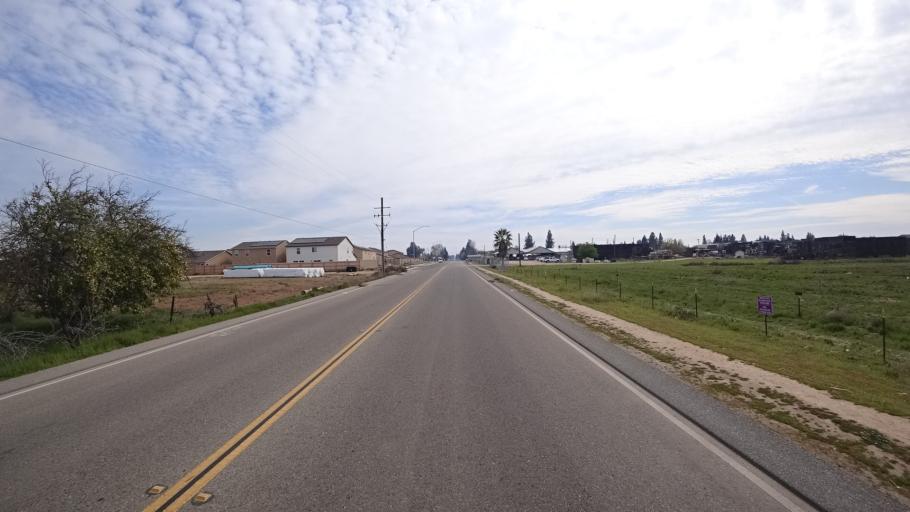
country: US
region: California
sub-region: Fresno County
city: West Park
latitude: 36.7863
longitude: -119.8924
